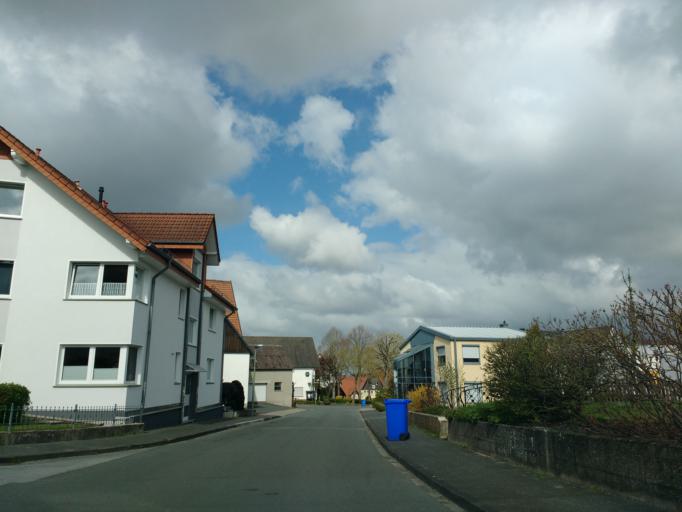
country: DE
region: North Rhine-Westphalia
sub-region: Regierungsbezirk Detmold
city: Wunnenberg
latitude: 51.5133
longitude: 8.7430
